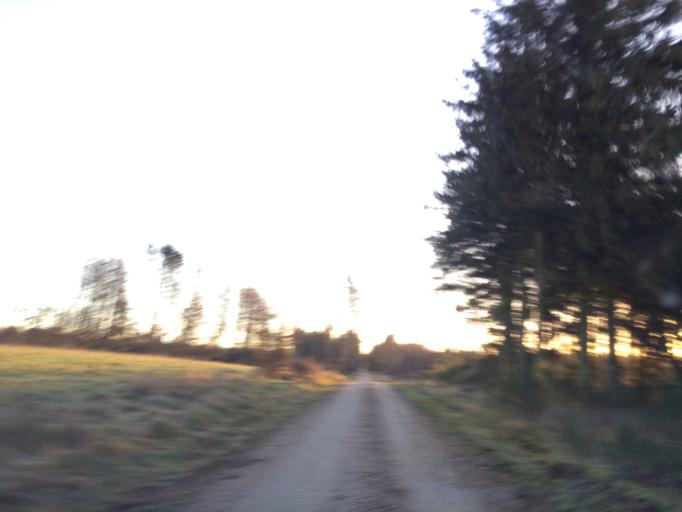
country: DK
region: Central Jutland
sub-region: Holstebro Kommune
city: Ulfborg
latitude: 56.2358
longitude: 8.4773
